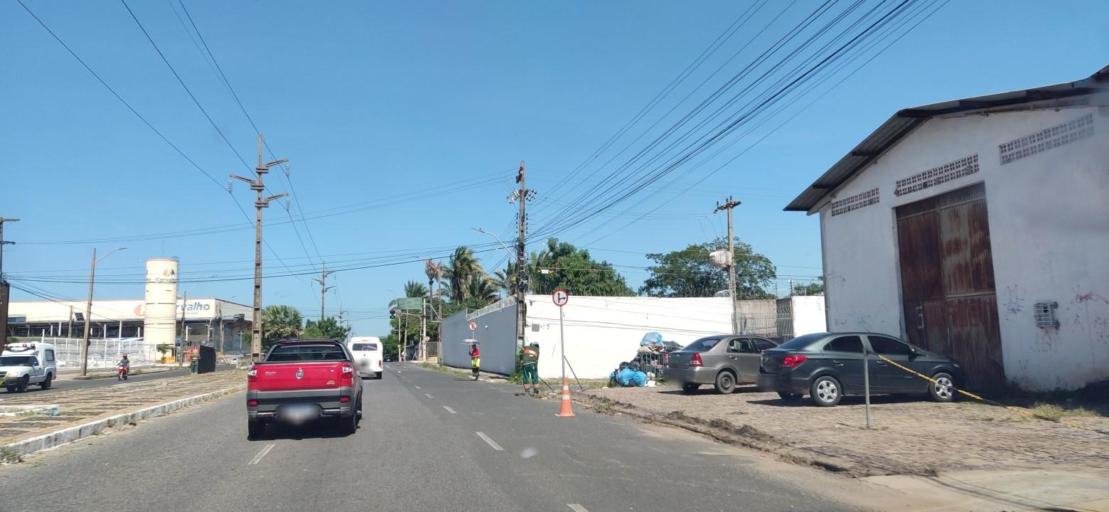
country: BR
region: Piaui
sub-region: Teresina
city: Teresina
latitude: -5.1189
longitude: -42.8022
